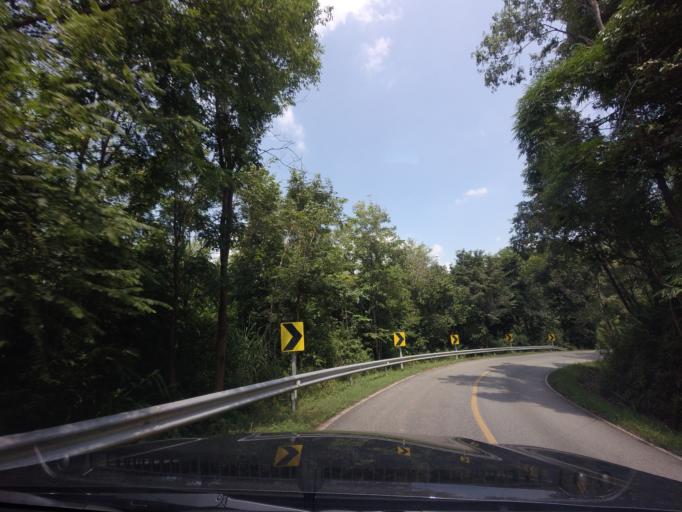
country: TH
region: Loei
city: Na Haeo
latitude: 17.6089
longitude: 100.8934
